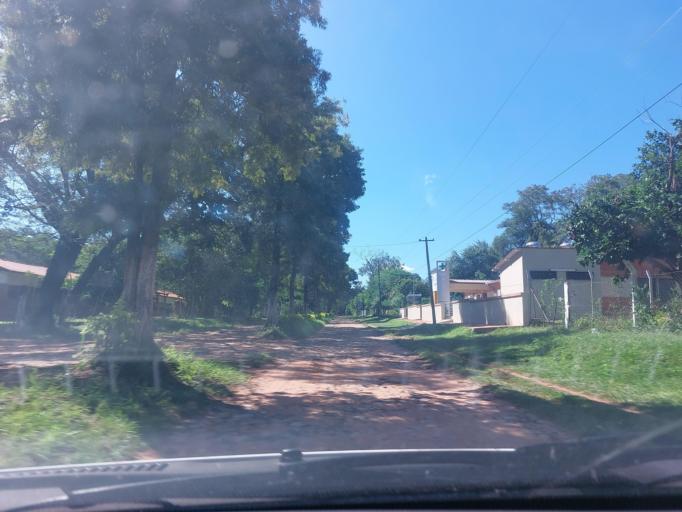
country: PY
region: San Pedro
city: Itacurubi del Rosario
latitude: -24.5599
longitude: -56.5908
